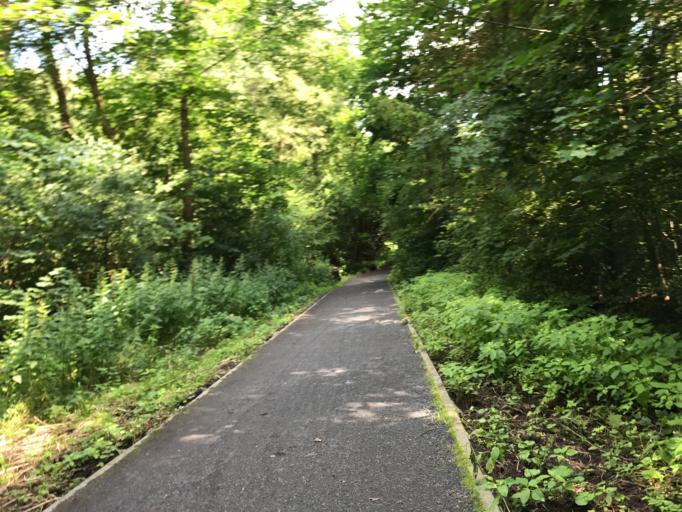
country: DE
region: Berlin
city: Hermsdorf
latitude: 52.6182
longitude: 13.3320
